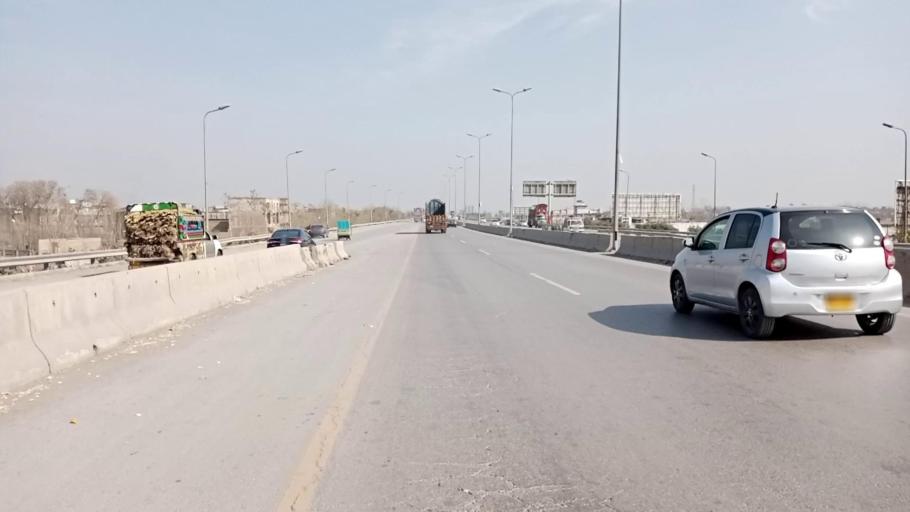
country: PK
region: Khyber Pakhtunkhwa
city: Peshawar
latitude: 34.0243
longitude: 71.6238
